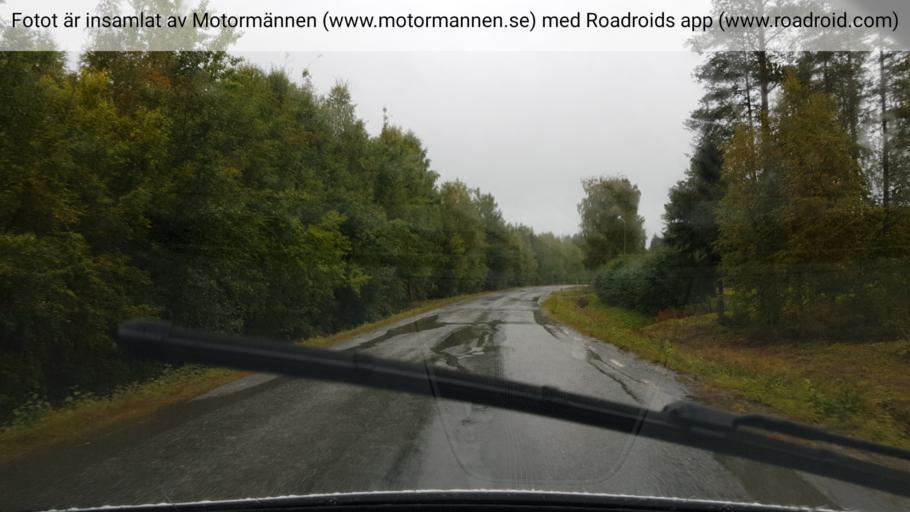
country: SE
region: Vaesterbotten
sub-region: Vannas Kommun
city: Vannasby
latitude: 64.0246
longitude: 19.9304
